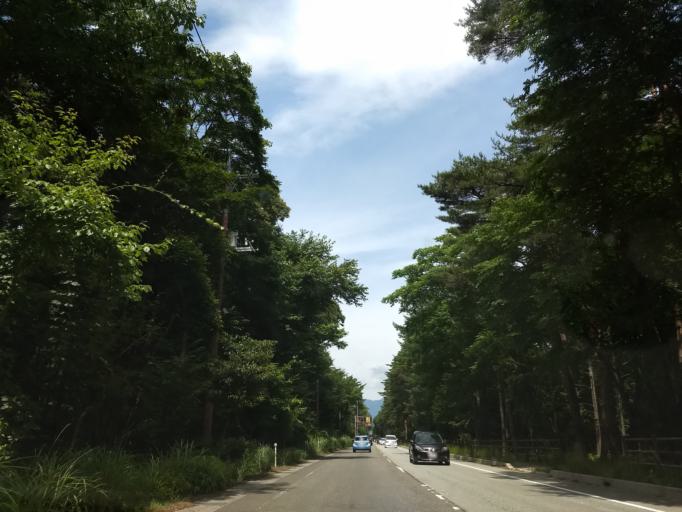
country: JP
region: Yamanashi
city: Fujikawaguchiko
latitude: 35.4446
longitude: 138.8262
